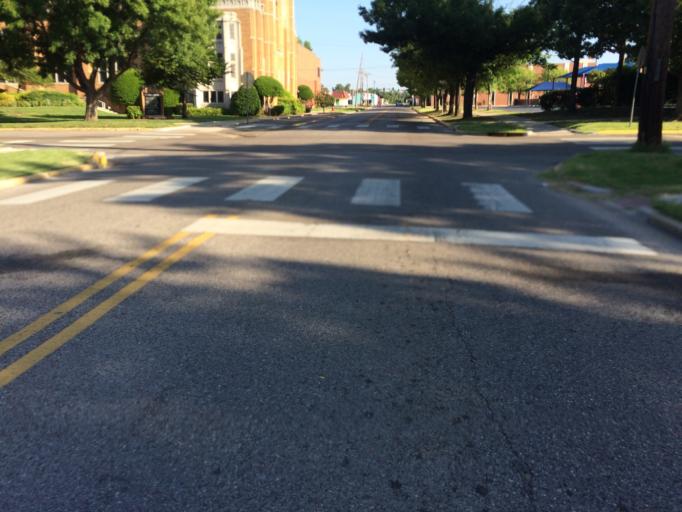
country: US
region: Oklahoma
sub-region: Cleveland County
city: Norman
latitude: 35.2174
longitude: -97.4454
